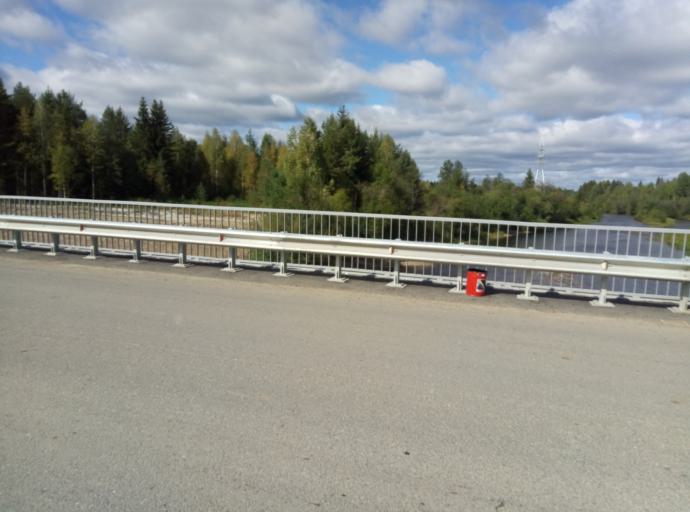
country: RU
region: Sverdlovsk
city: Karpinsk
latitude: 59.6707
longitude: 59.7851
